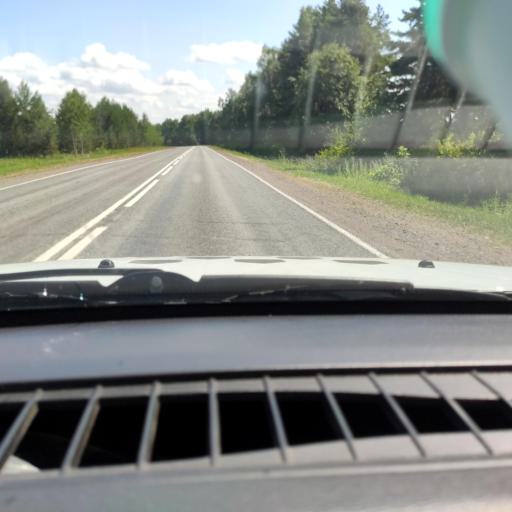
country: RU
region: Bashkortostan
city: Mesyagutovo
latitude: 55.4763
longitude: 58.3430
